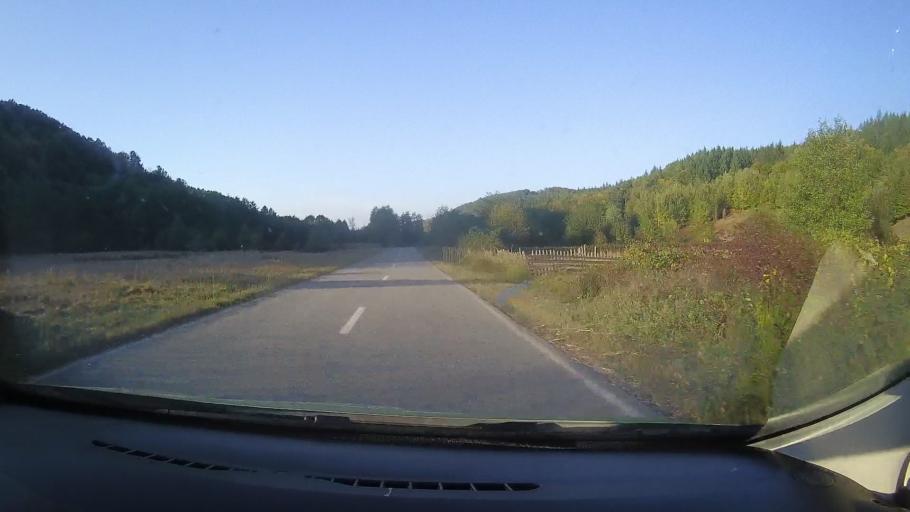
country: RO
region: Timis
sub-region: Comuna Fardea
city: Fardea
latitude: 45.7030
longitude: 22.1604
